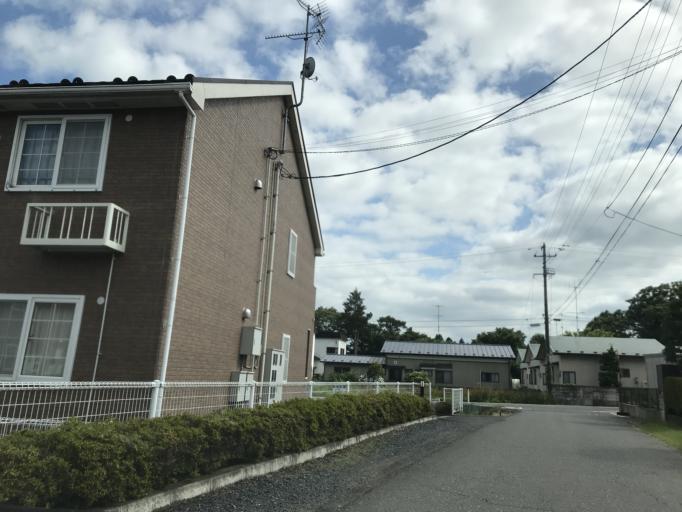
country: JP
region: Iwate
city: Ichinoseki
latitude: 38.9292
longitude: 141.0967
